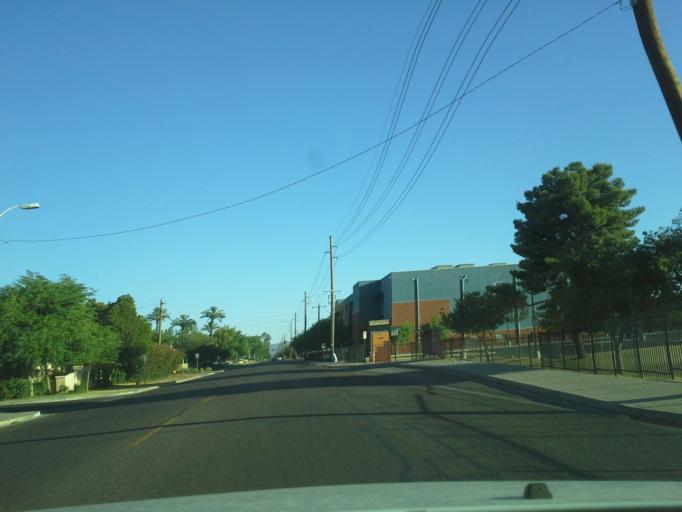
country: US
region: Arizona
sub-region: Maricopa County
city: Phoenix
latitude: 33.5059
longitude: -112.0217
